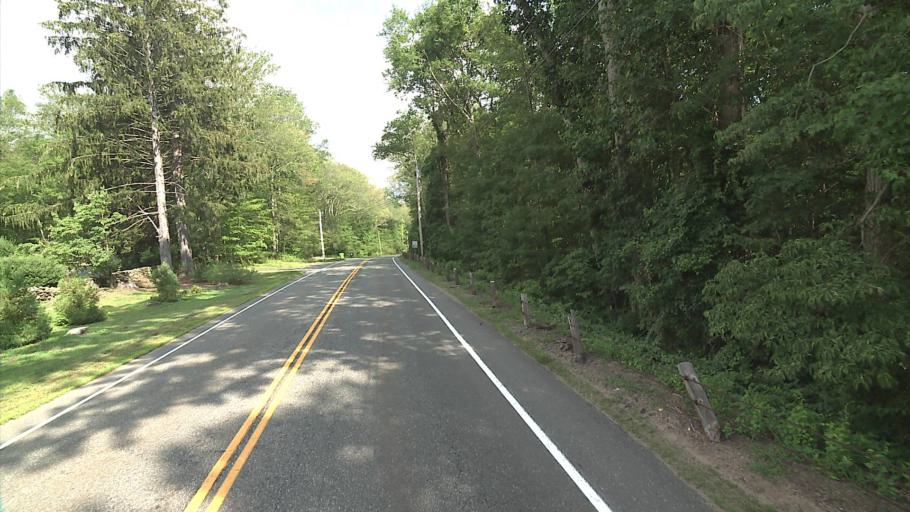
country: US
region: Connecticut
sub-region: Middlesex County
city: Chester Center
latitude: 41.3784
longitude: -72.5074
